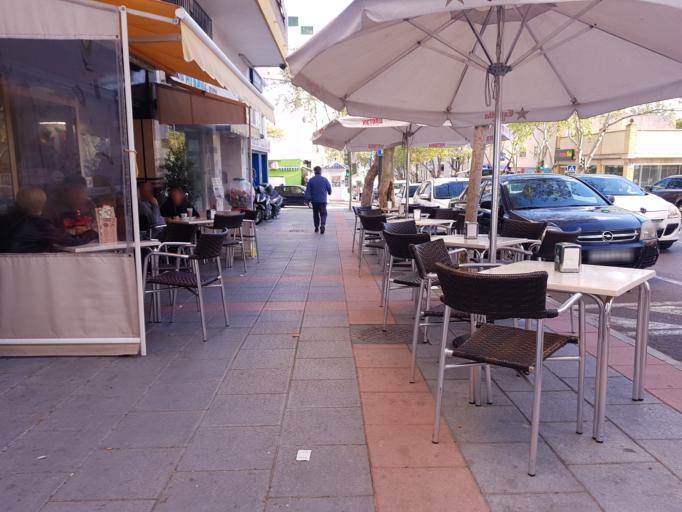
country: ES
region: Andalusia
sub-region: Provincia de Malaga
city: Marbella
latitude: 36.5144
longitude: -4.8769
